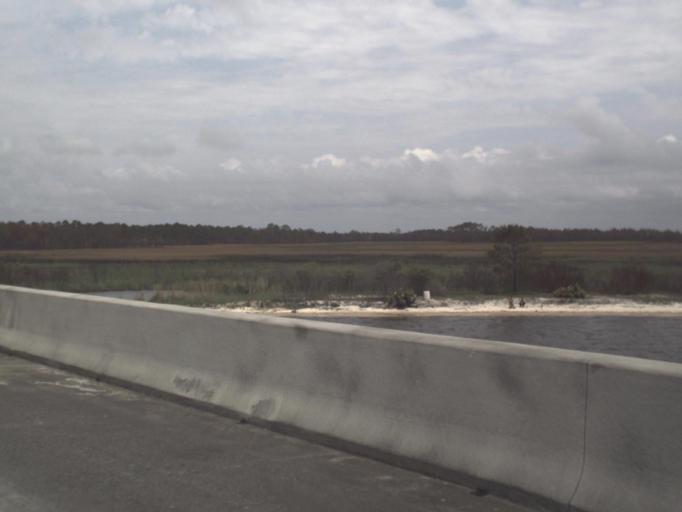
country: US
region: Florida
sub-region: Santa Rosa County
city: Oriole Beach
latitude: 30.4430
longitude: -87.1006
